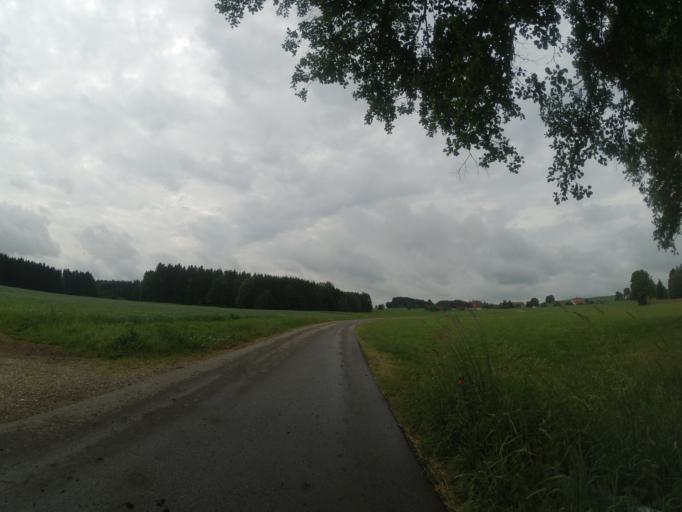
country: DE
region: Baden-Wuerttemberg
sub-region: Tuebingen Region
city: Kisslegg
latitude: 47.7529
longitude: 9.8531
